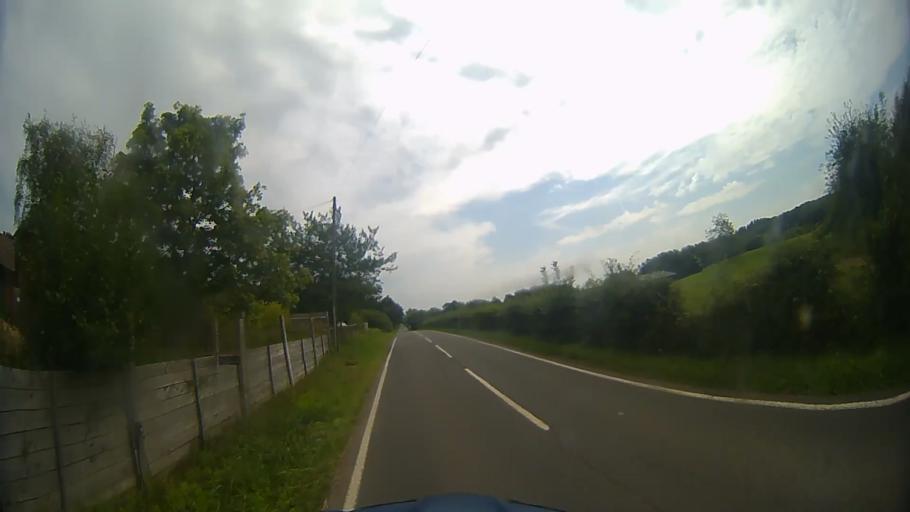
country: GB
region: England
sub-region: Hampshire
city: Kingsley
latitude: 51.1717
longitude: -0.8642
